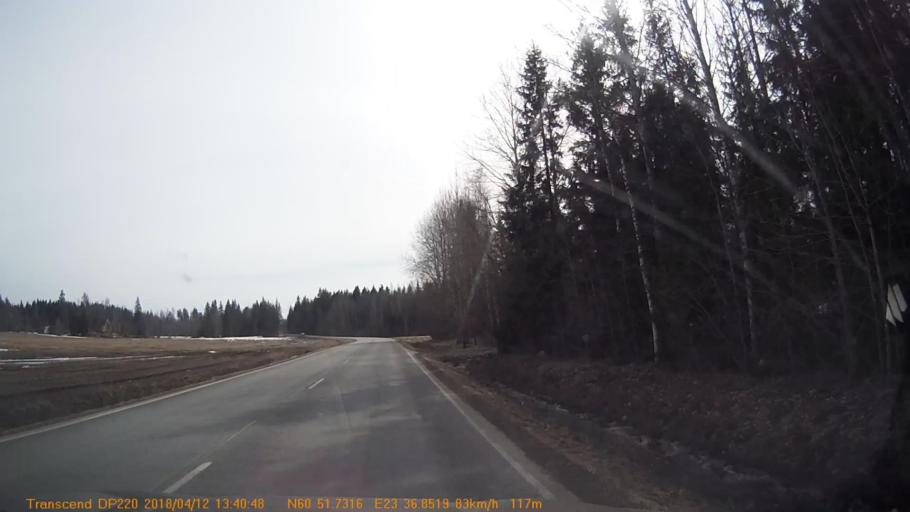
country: FI
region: Haeme
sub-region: Forssa
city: Forssa
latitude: 60.8615
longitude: 23.6144
